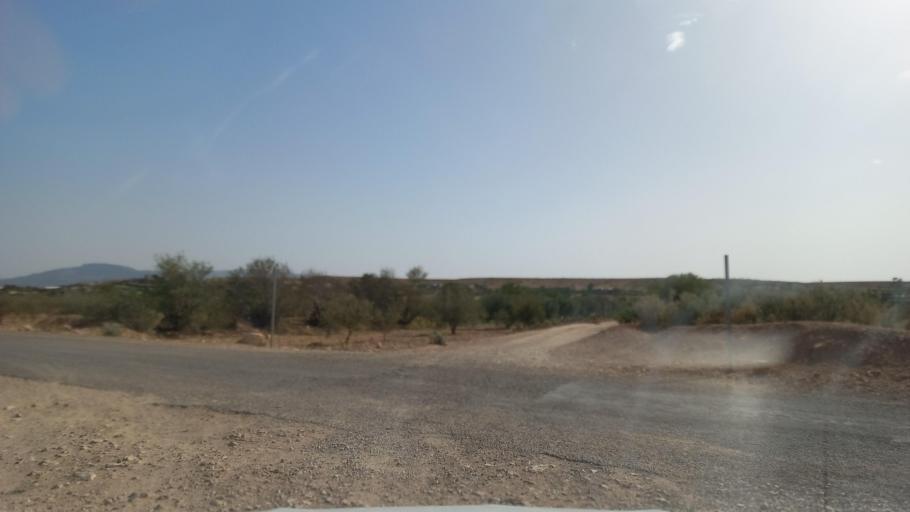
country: TN
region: Al Qasrayn
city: Kasserine
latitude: 35.2659
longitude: 8.9335
